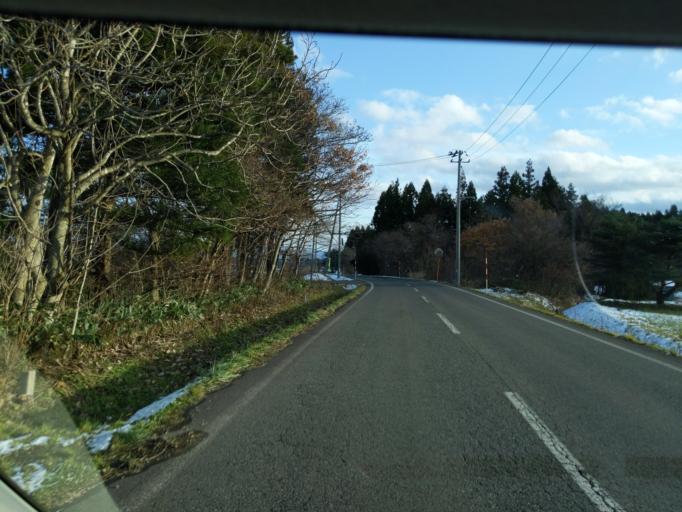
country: JP
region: Iwate
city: Kitakami
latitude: 39.2229
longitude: 141.0156
